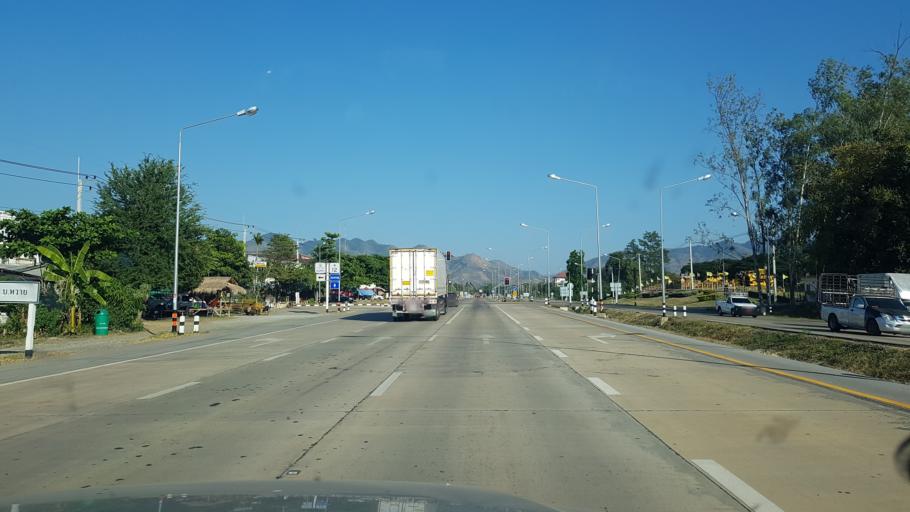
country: TH
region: Phetchabun
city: Lom Sak
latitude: 16.7284
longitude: 101.2841
